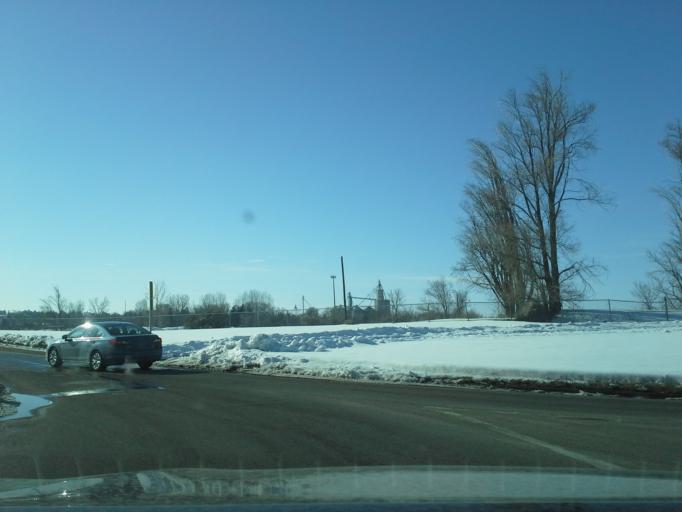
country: US
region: Idaho
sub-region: Bonneville County
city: Idaho Falls
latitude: 43.5093
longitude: -112.0472
